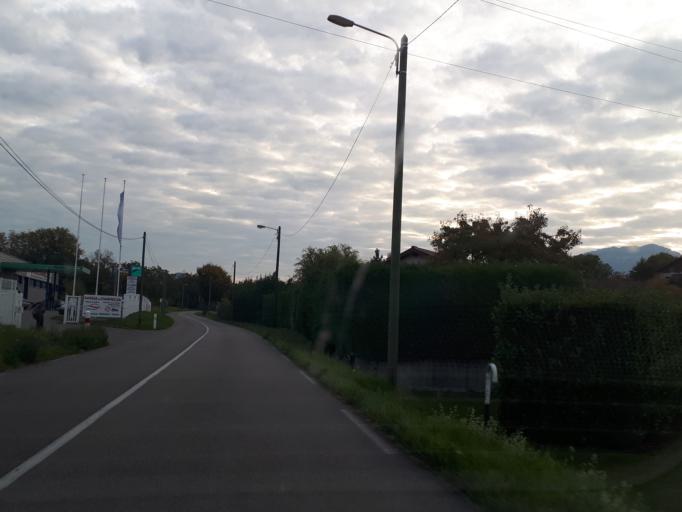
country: FR
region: Rhone-Alpes
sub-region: Departement de l'Isere
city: Charnecles
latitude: 45.3490
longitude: 5.5289
